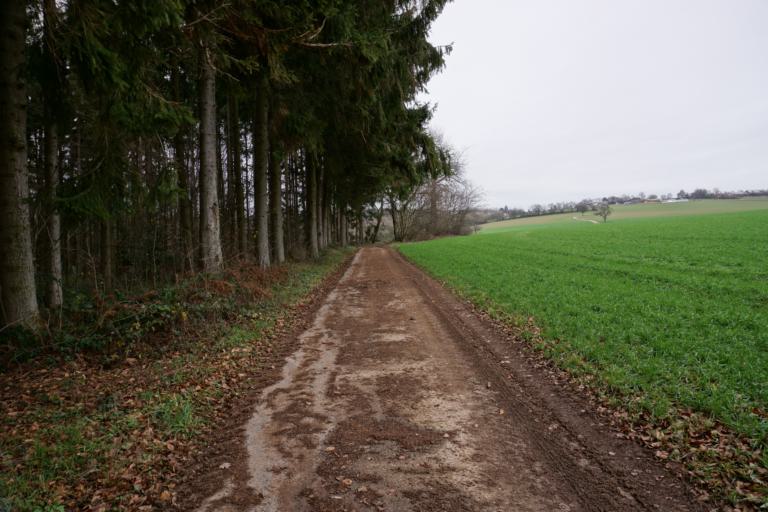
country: DE
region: Baden-Wuerttemberg
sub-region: Karlsruhe Region
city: Neckargerach
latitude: 49.4219
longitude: 9.0808
